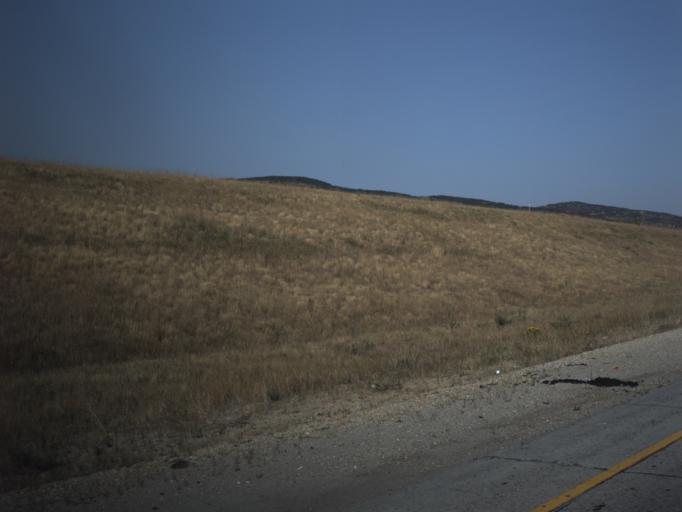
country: US
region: Utah
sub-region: Summit County
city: Park City
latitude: 40.6842
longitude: -111.4617
